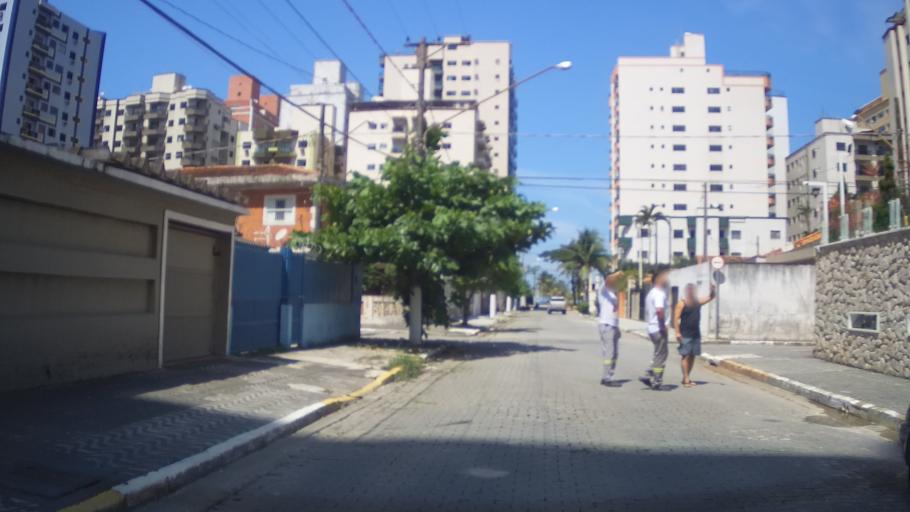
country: BR
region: Sao Paulo
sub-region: Praia Grande
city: Praia Grande
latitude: -24.0171
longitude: -46.4429
